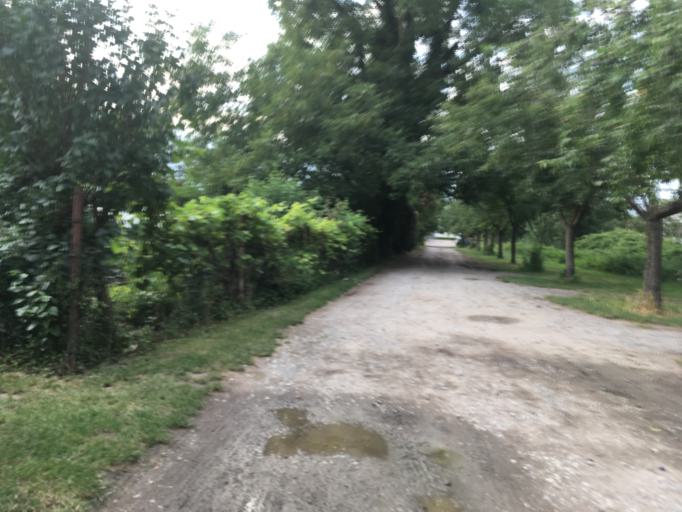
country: DE
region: Rheinland-Pfalz
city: Otterstadt
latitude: 49.3707
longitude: 8.4579
